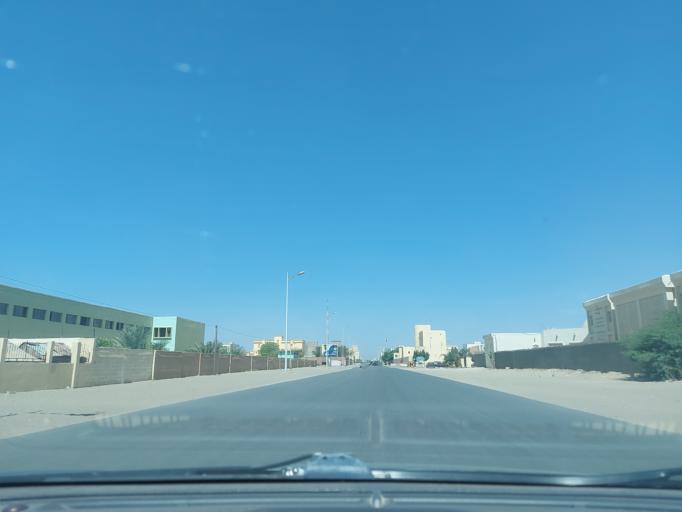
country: MR
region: Nouakchott
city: Nouakchott
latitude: 18.0806
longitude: -15.9715
